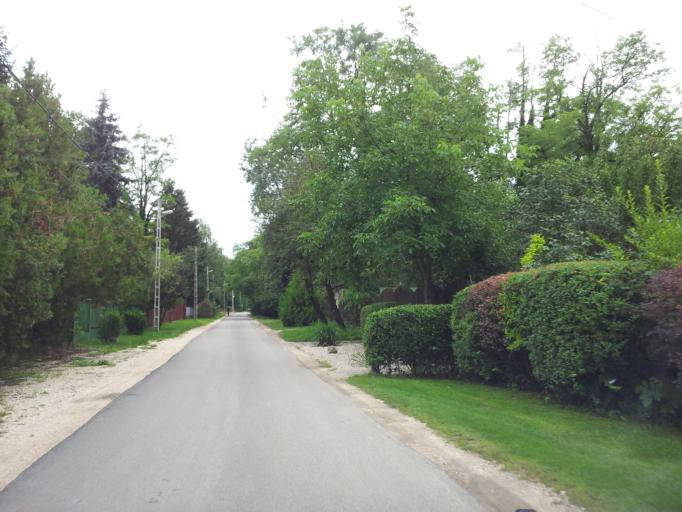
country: HU
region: Pest
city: Szigetujfalu
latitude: 47.2086
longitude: 18.9626
